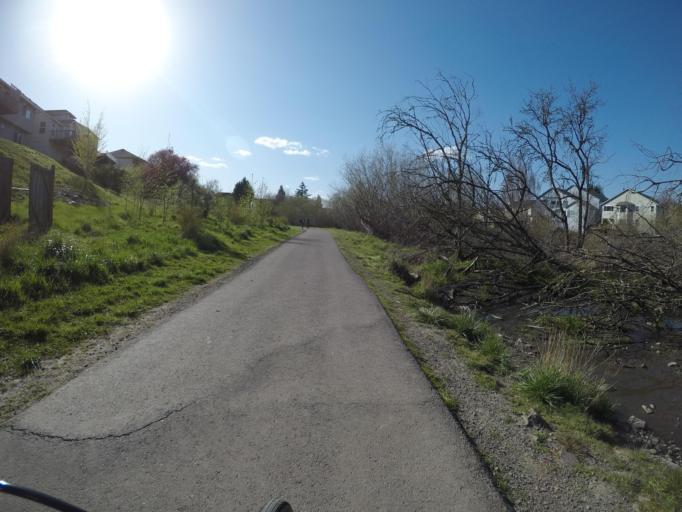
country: US
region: Oregon
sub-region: Washington County
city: Bethany
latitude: 45.5571
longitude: -122.8525
